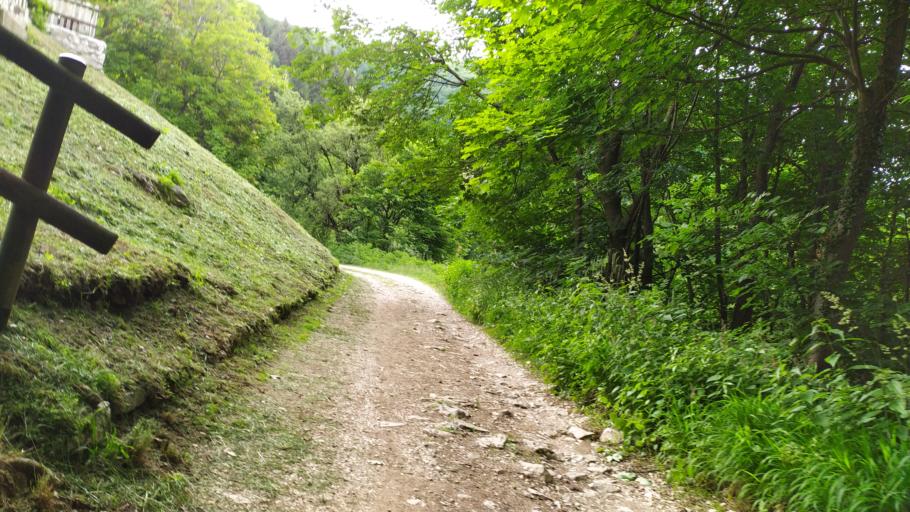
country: IT
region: Veneto
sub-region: Provincia di Vicenza
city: Torrebelvicino
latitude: 45.6847
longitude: 11.3079
